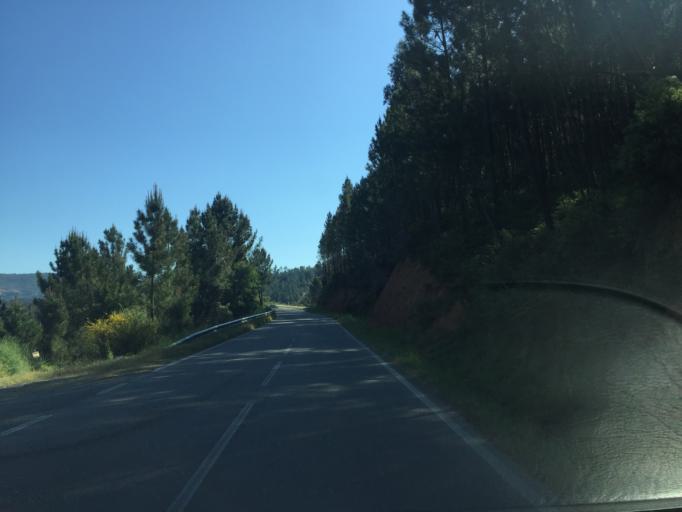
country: PT
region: Coimbra
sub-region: Pampilhosa da Serra
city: Pampilhosa da Serra
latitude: 40.0564
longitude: -7.8031
